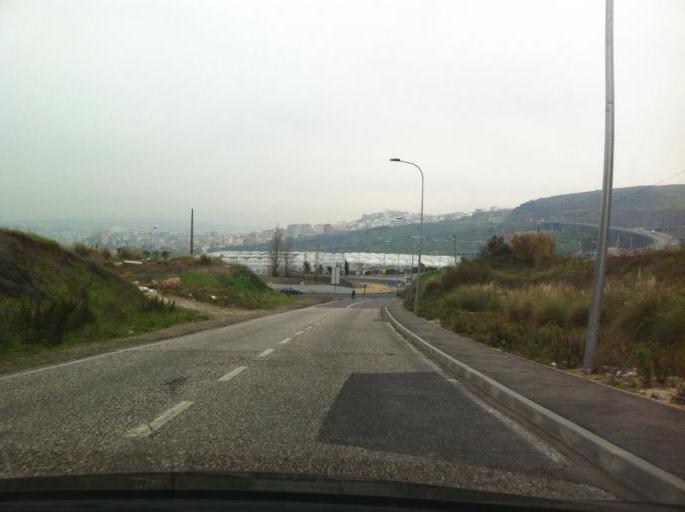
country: PT
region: Lisbon
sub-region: Odivelas
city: Famoes
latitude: 38.7824
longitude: -9.2210
